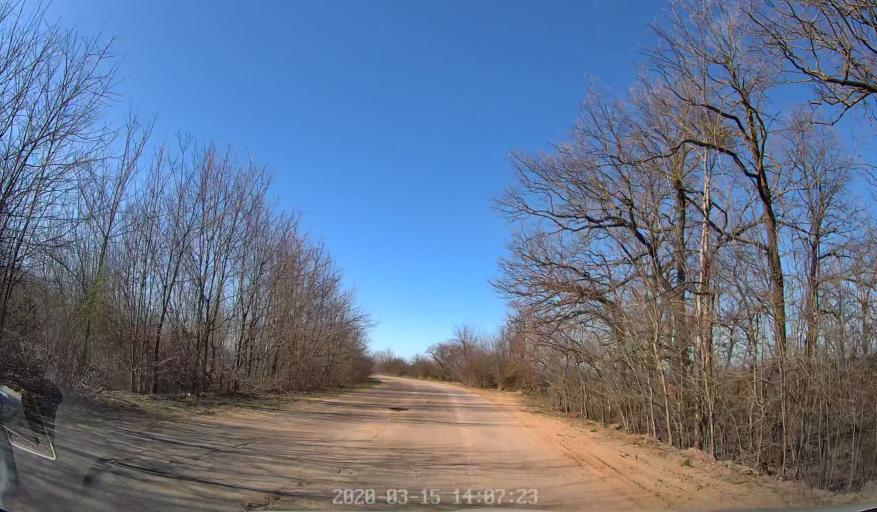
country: MD
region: Orhei
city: Orhei
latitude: 47.3029
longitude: 28.9483
